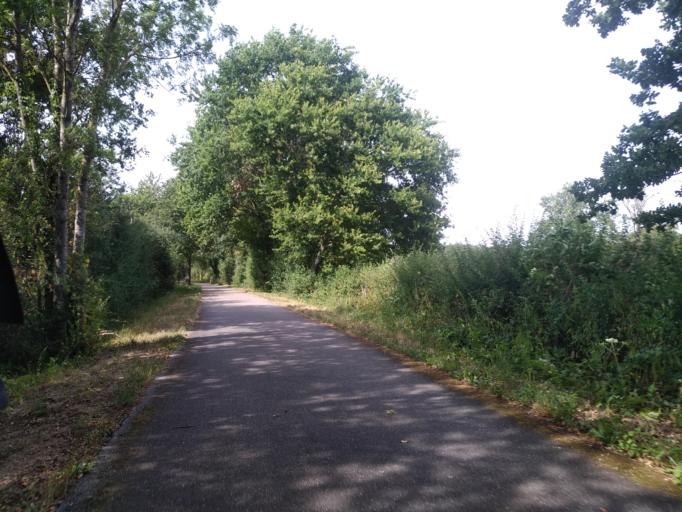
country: FR
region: Bourgogne
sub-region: Departement de Saone-et-Loire
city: Bourbon-Lancy
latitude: 46.6038
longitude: 3.7461
